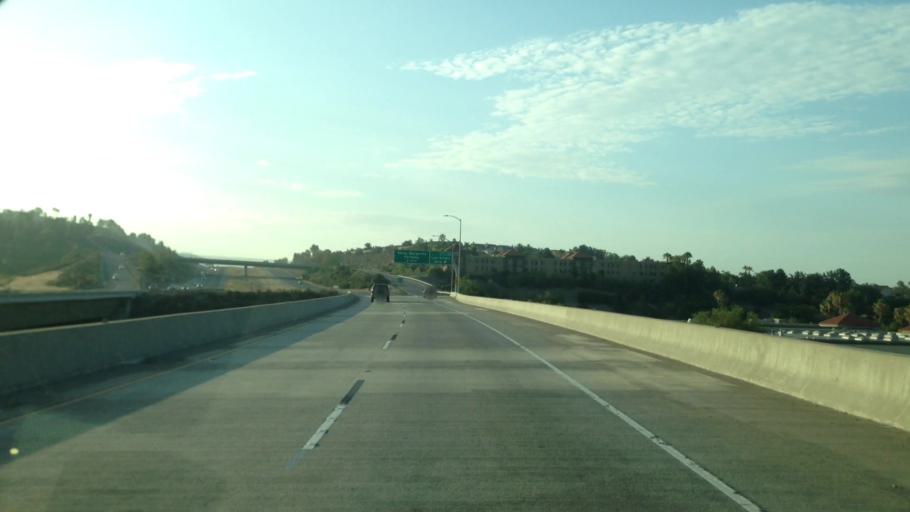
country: US
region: California
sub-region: Orange County
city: Portola Hills
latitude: 33.6571
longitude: -117.6313
